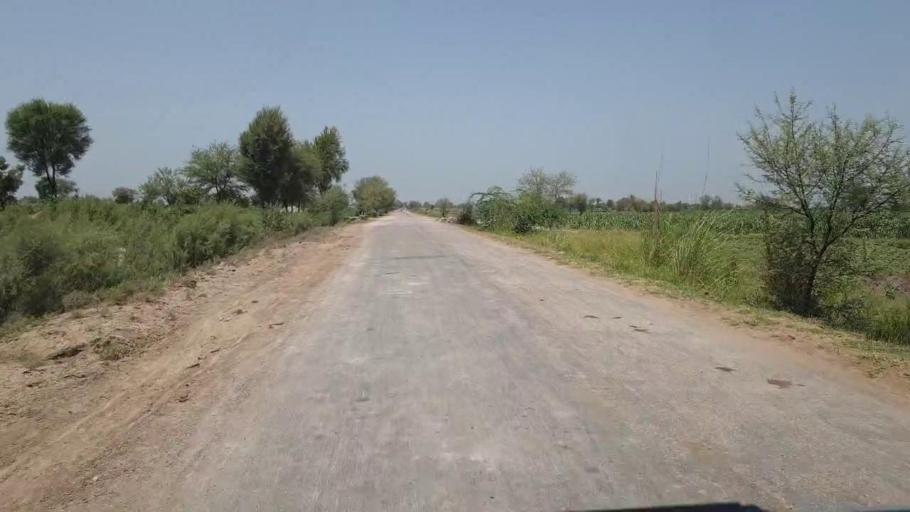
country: PK
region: Sindh
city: Nawabshah
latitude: 26.3521
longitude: 68.3951
